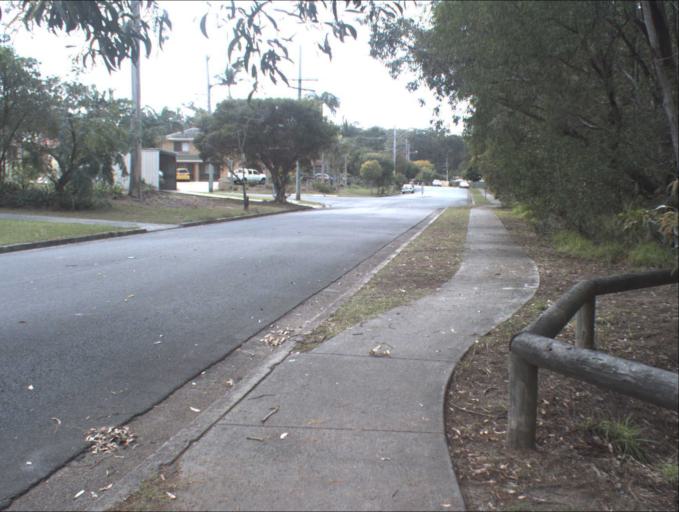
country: AU
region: Queensland
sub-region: Brisbane
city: Sunnybank Hills
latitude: -27.6573
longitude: 153.0428
